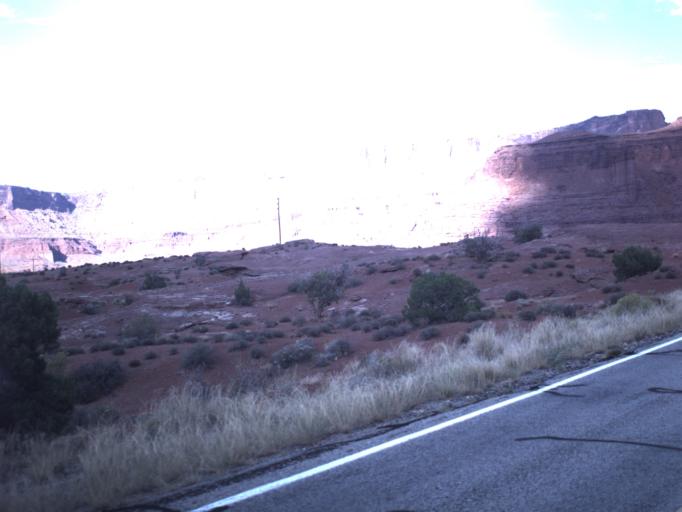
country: US
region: Utah
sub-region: Grand County
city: Moab
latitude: 38.7397
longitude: -109.3351
